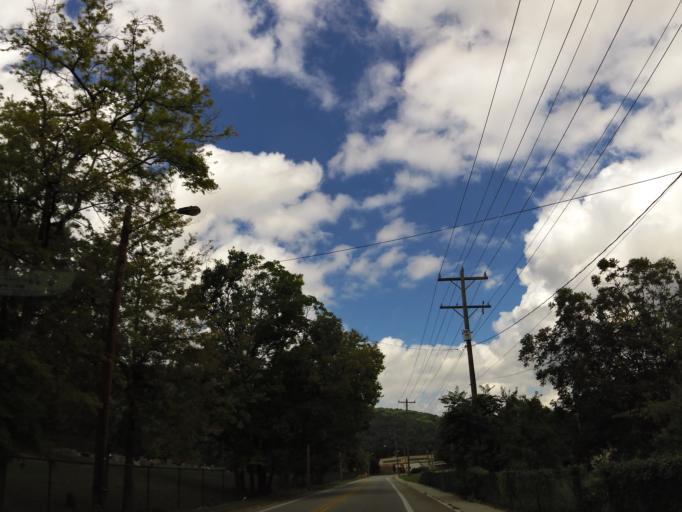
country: US
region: Tennessee
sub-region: Hamilton County
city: Lookout Mountain
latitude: 35.0075
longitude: -85.3193
